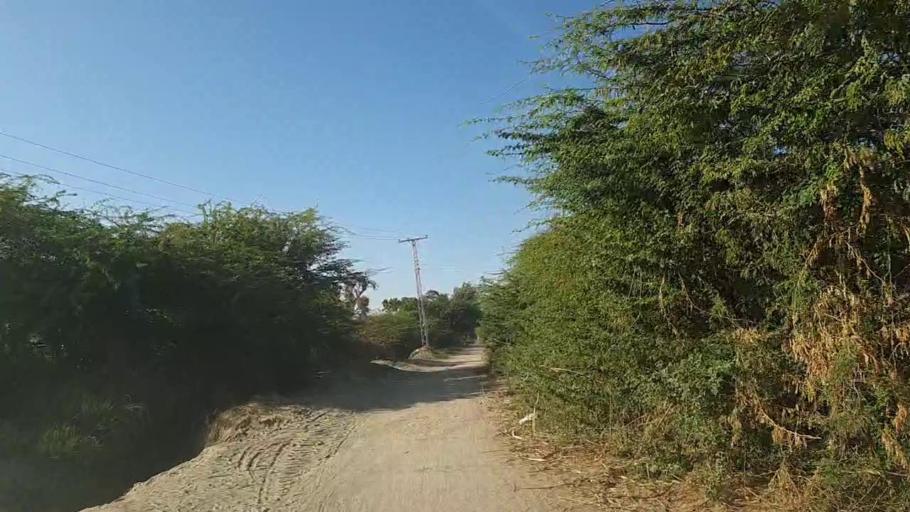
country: PK
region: Sindh
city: Samaro
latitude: 25.2656
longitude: 69.4850
